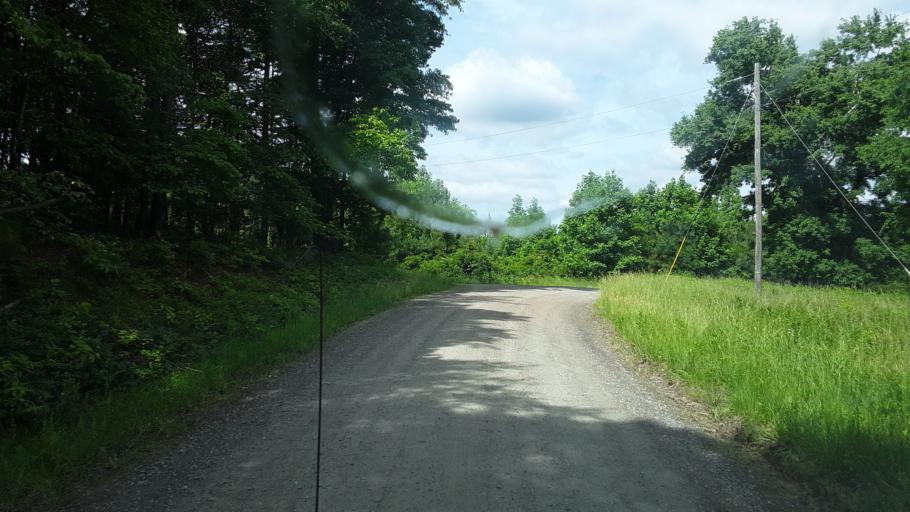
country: US
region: Virginia
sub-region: Pittsylvania County
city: Chatham
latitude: 36.8515
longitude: -79.4352
